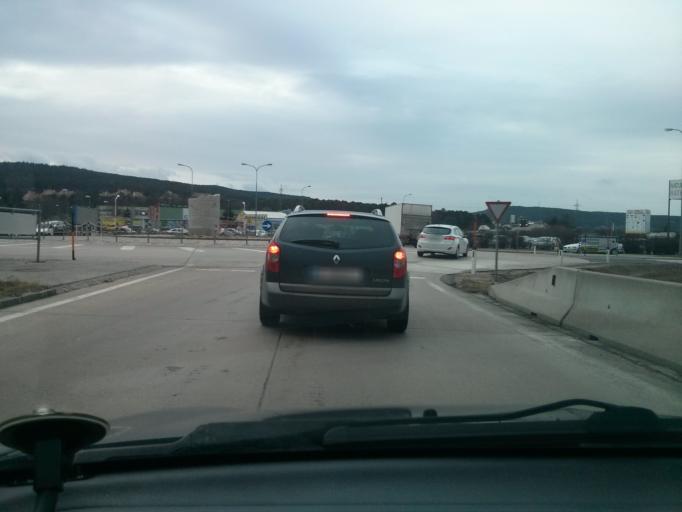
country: AT
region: Lower Austria
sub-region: Politischer Bezirk Wiener Neustadt
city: Theresienfeld
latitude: 47.8502
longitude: 16.1938
